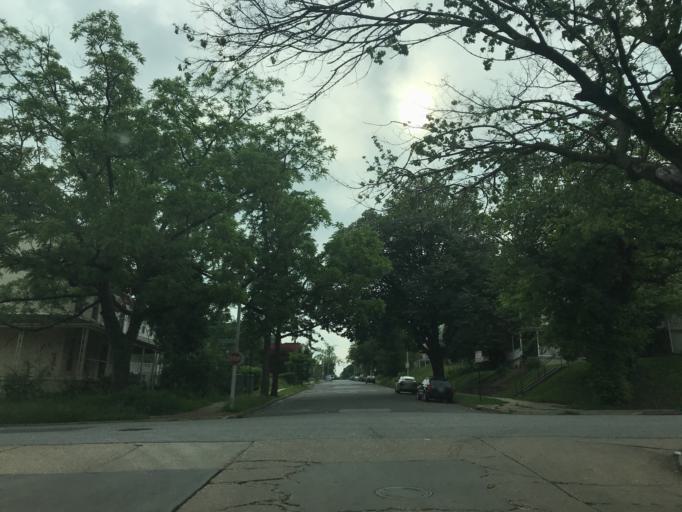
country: US
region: Maryland
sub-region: City of Baltimore
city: Baltimore
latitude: 39.3102
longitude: -76.6637
